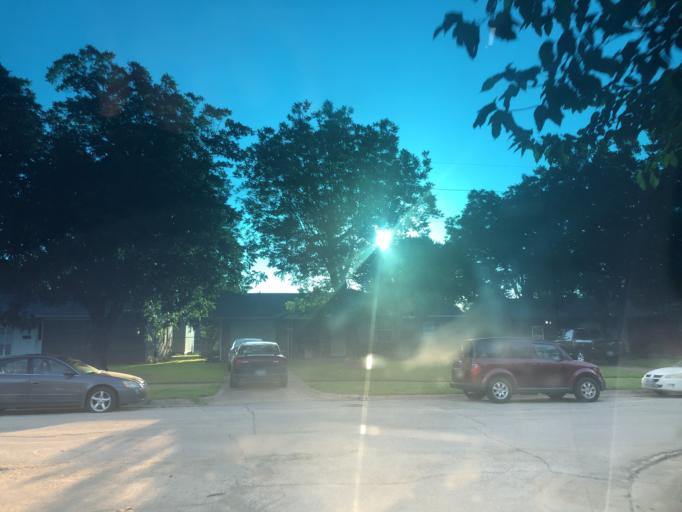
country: US
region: Texas
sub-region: Dallas County
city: Grand Prairie
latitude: 32.7067
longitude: -97.0133
